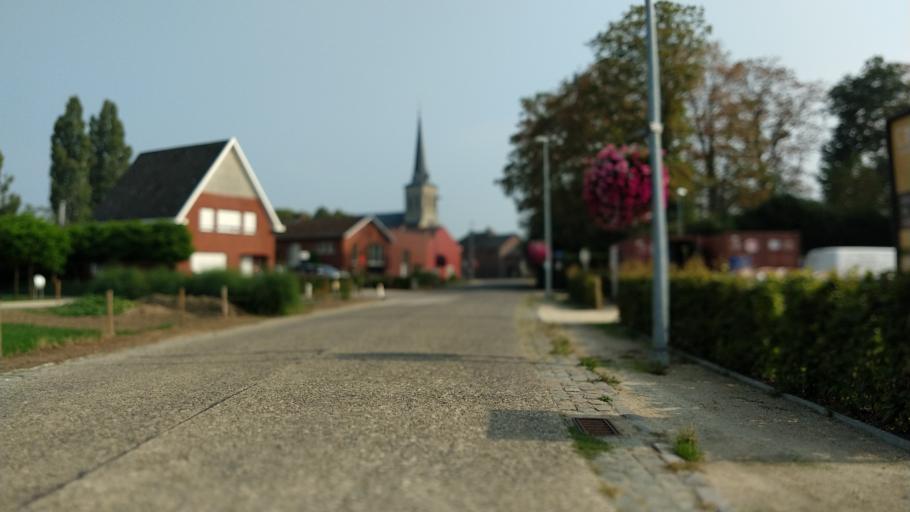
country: BE
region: Flanders
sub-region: Provincie Vlaams-Brabant
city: Rotselaar
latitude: 50.9571
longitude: 4.6776
